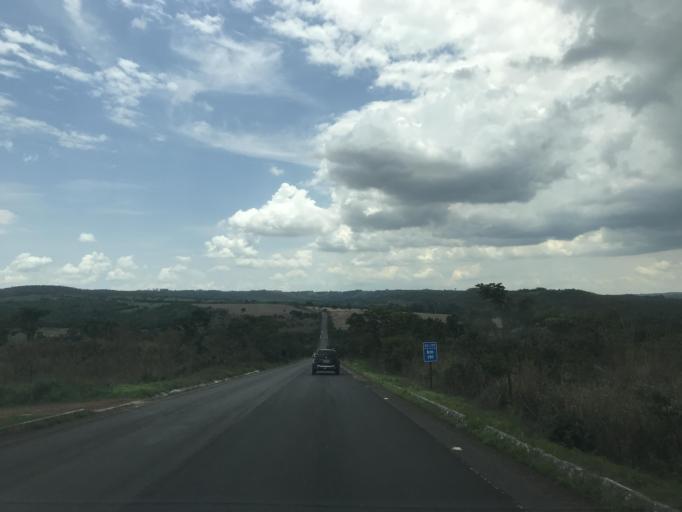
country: BR
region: Goias
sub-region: Vianopolis
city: Vianopolis
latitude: -16.9475
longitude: -48.5746
